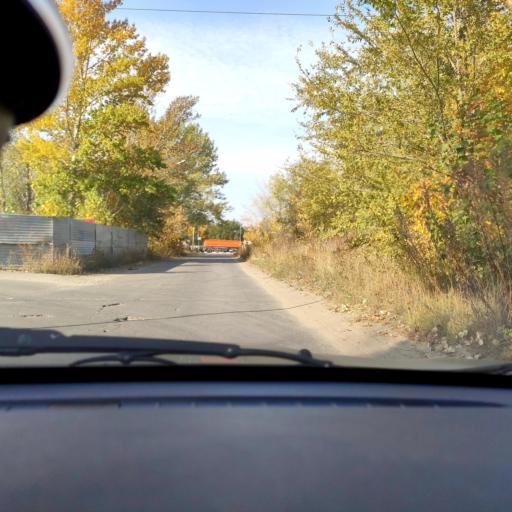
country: RU
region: Samara
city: Tol'yatti
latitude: 53.5495
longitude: 49.2851
